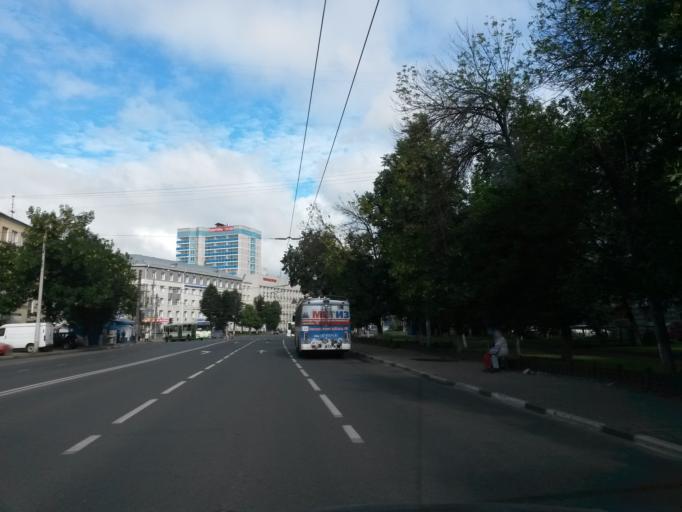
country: RU
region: Jaroslavl
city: Yaroslavl
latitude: 57.6395
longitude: 39.8768
